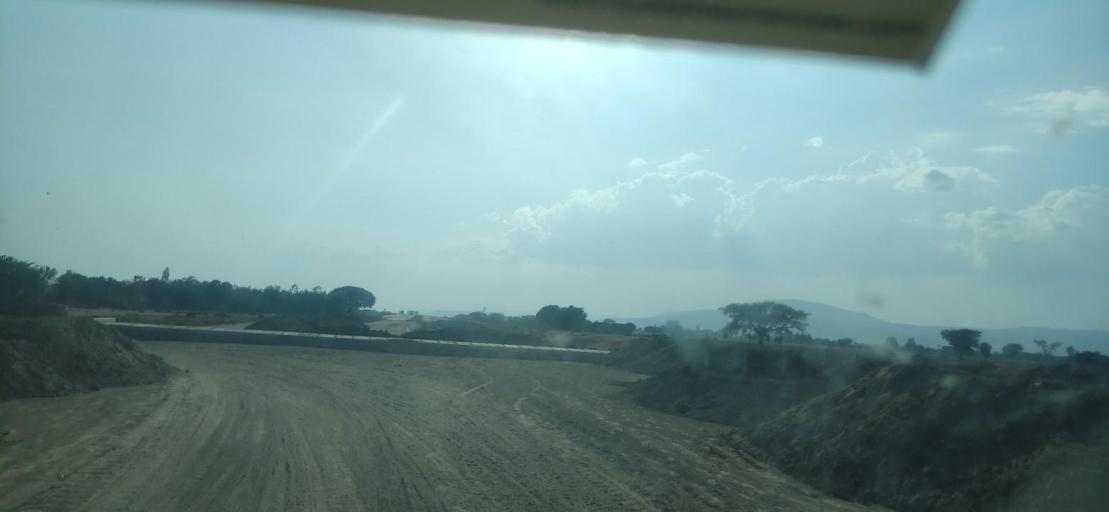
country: ET
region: Oromiya
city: Shashemene
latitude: 7.2047
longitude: 38.5419
